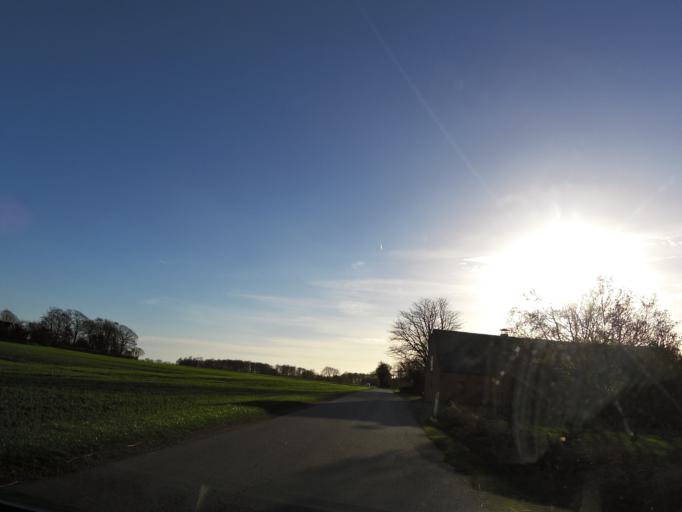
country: DK
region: Central Jutland
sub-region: Odder Kommune
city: Odder
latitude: 55.9244
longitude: 10.2342
